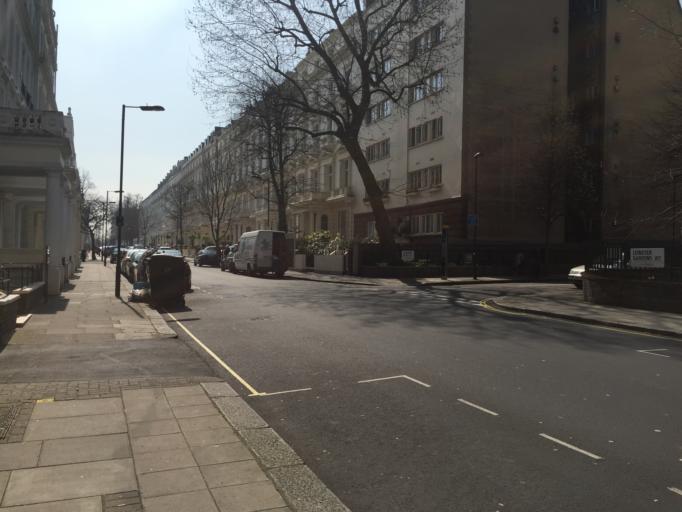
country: GB
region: England
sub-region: Greater London
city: Bayswater
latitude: 51.5146
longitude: -0.1840
